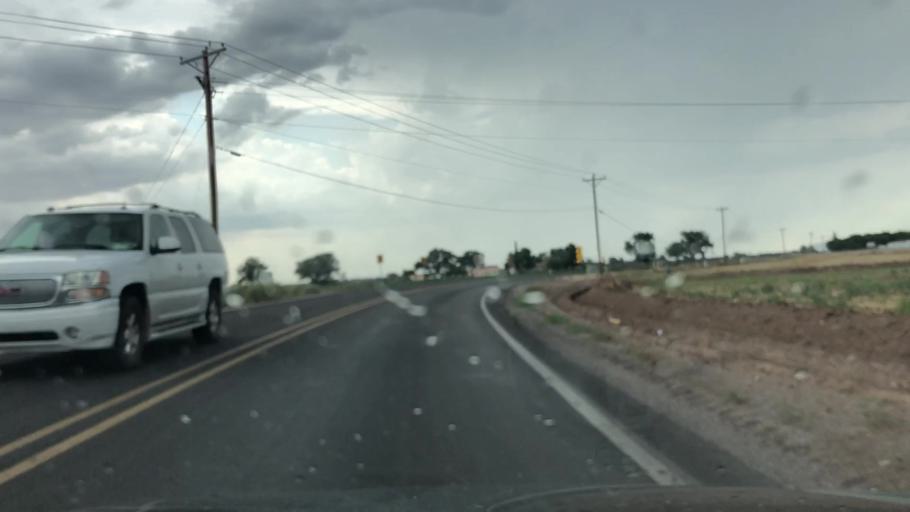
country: US
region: New Mexico
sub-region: Dona Ana County
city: Vado
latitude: 32.0713
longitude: -106.6832
